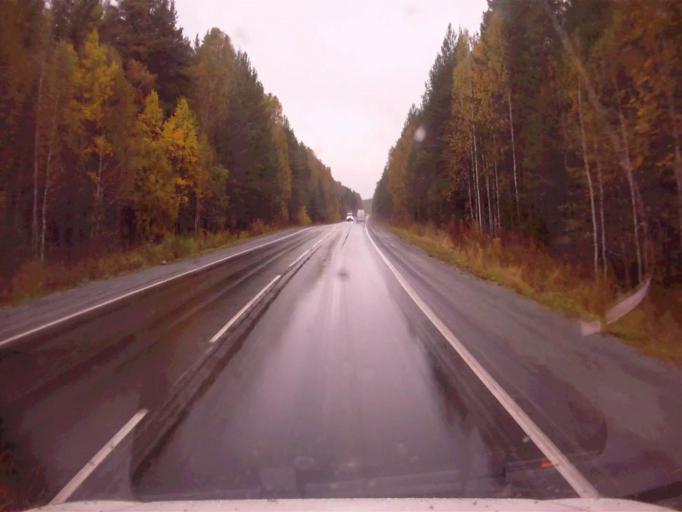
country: RU
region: Chelyabinsk
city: Tayginka
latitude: 55.5592
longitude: 60.6469
